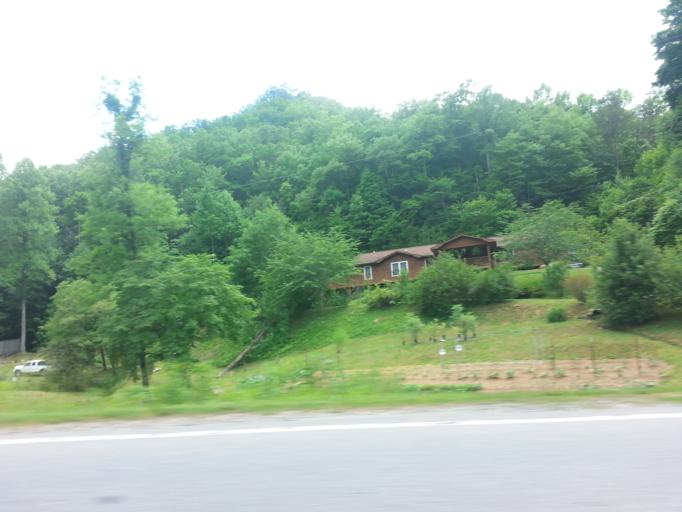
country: US
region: North Carolina
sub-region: Cherokee County
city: Andrews
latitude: 35.2283
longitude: -83.7353
